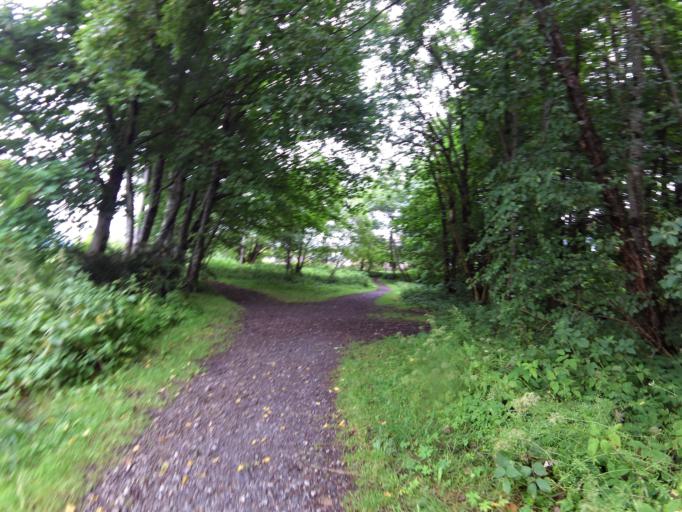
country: GB
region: Scotland
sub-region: Highland
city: Fort William
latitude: 56.8251
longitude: -5.1003
